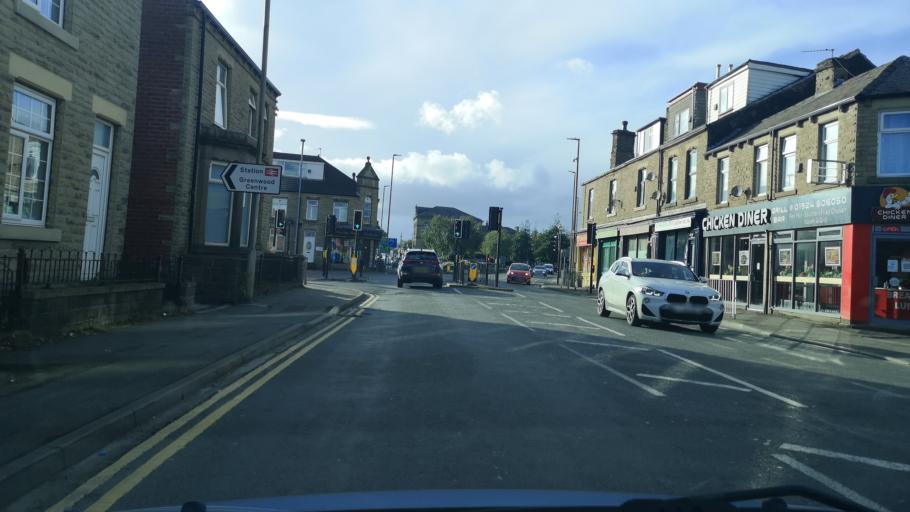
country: GB
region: England
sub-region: Kirklees
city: Heckmondwike
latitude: 53.6797
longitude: -1.6606
